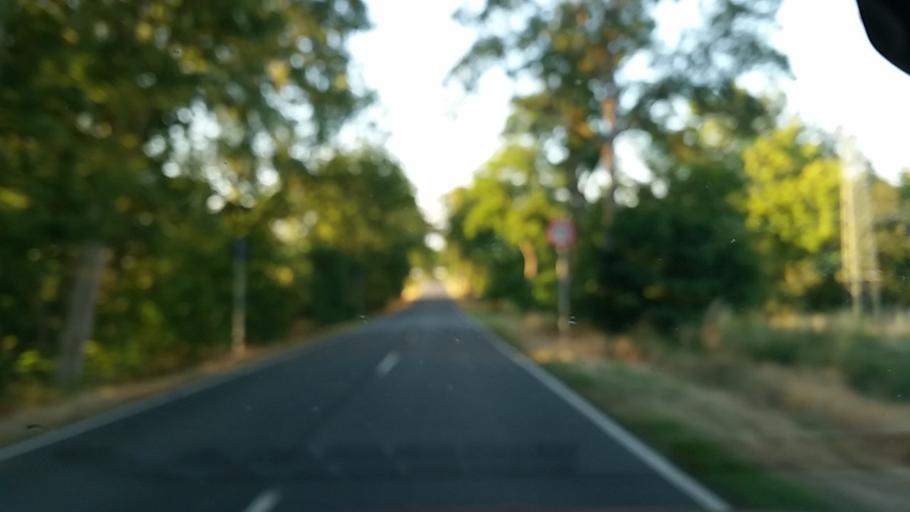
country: DE
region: Lower Saxony
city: Weyhausen
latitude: 52.4070
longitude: 10.7028
